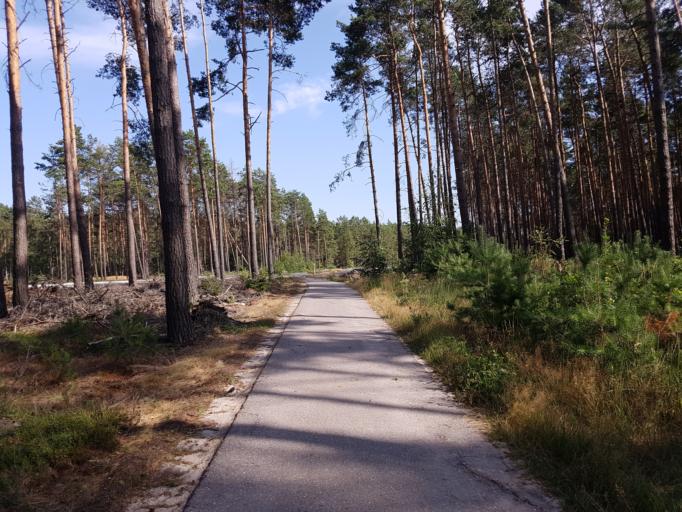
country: DE
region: Brandenburg
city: Finsterwalde
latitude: 51.6251
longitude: 13.6643
